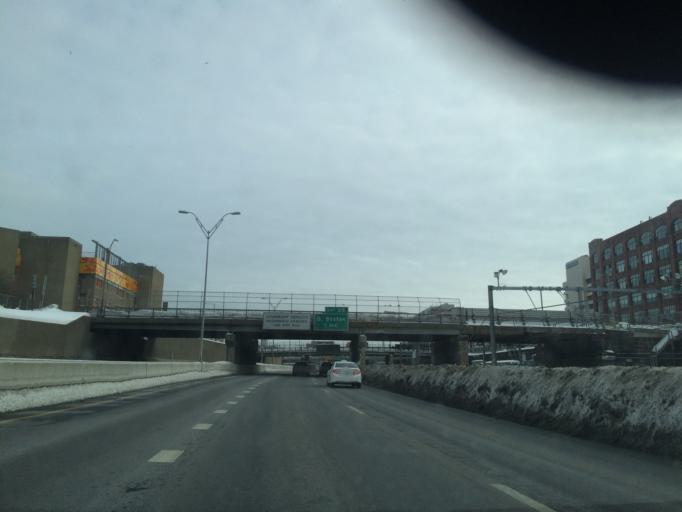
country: US
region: Massachusetts
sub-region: Suffolk County
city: Boston
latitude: 42.3476
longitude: -71.0668
